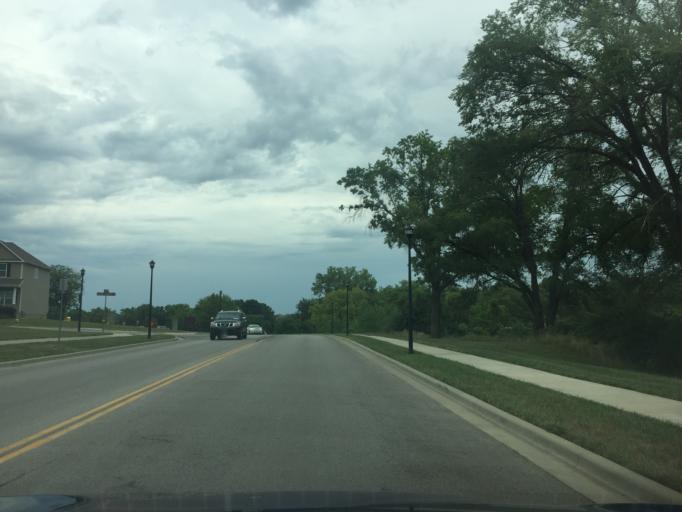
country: US
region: Kansas
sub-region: Leavenworth County
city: Leavenworth
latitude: 39.3438
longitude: -94.9331
